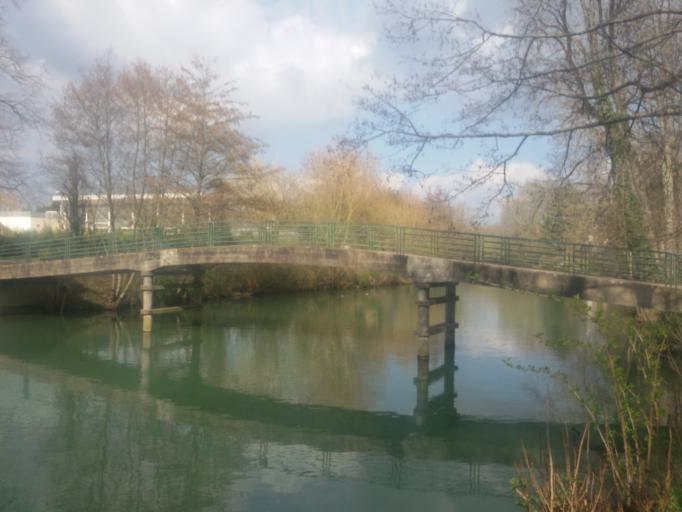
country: FR
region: Poitou-Charentes
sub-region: Departement des Deux-Sevres
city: Niort
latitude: 46.3307
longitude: -0.4622
